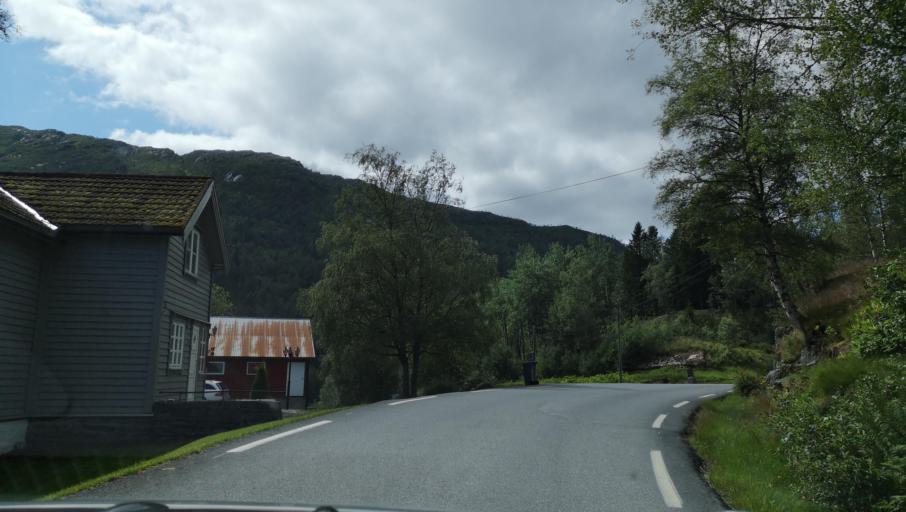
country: NO
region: Hordaland
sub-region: Modalen
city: Mo
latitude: 60.7839
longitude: 5.9218
